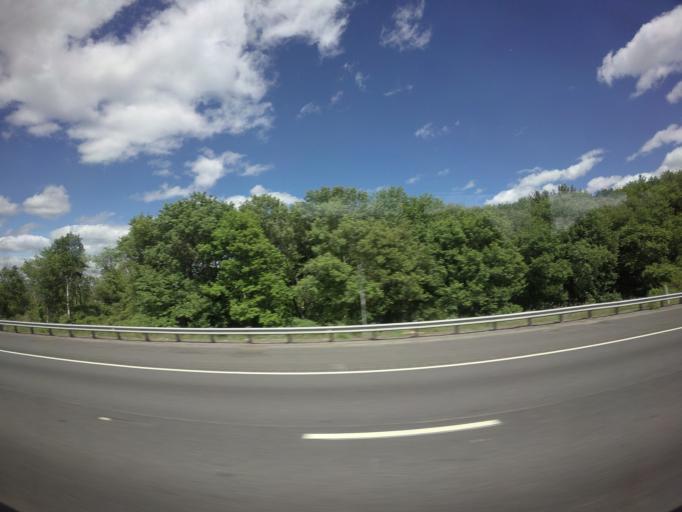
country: US
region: Massachusetts
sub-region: Middlesex County
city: Wilmington
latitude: 42.5492
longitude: -71.1365
